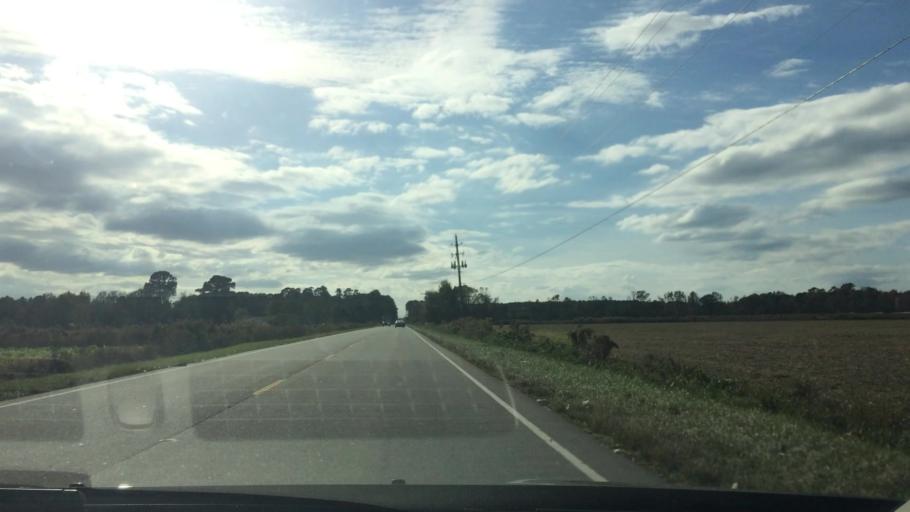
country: US
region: North Carolina
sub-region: Wayne County
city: Elroy
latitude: 35.4383
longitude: -77.8579
